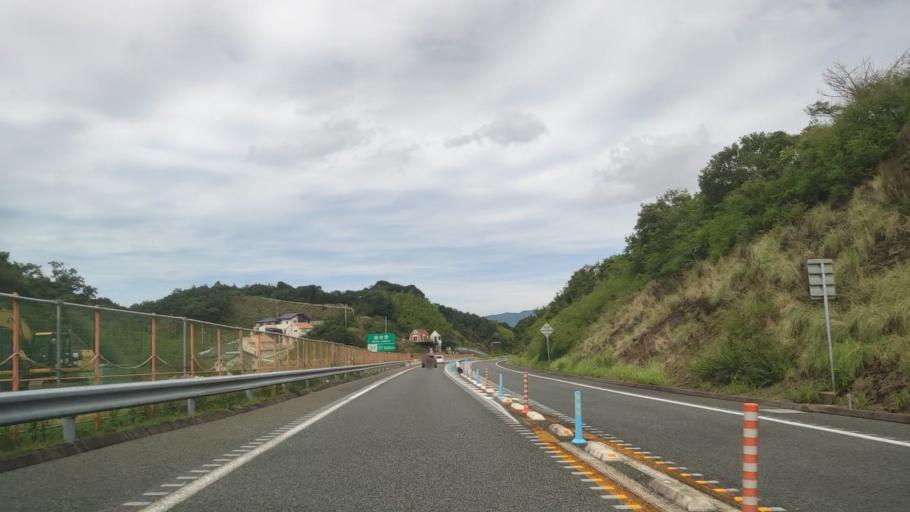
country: JP
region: Wakayama
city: Gobo
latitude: 33.8805
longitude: 135.1843
